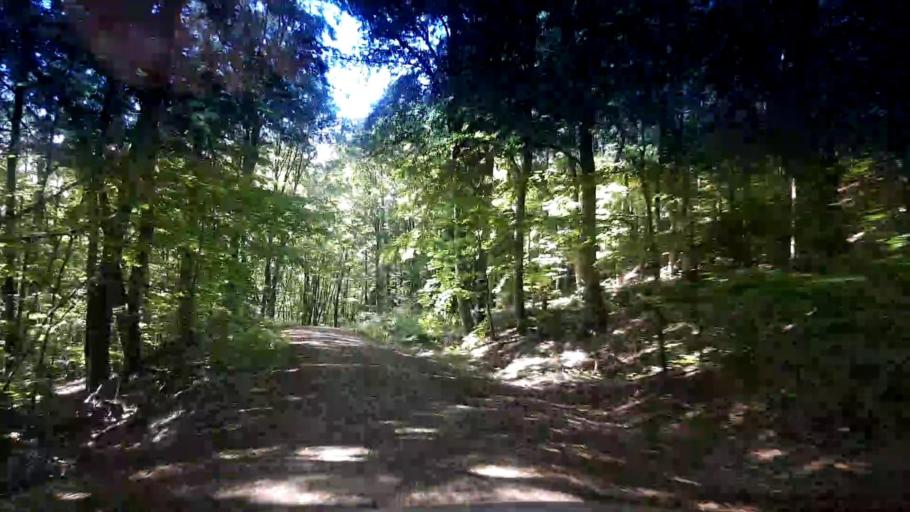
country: DE
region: Bavaria
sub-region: Upper Franconia
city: Litzendorf
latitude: 49.8845
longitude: 11.0225
